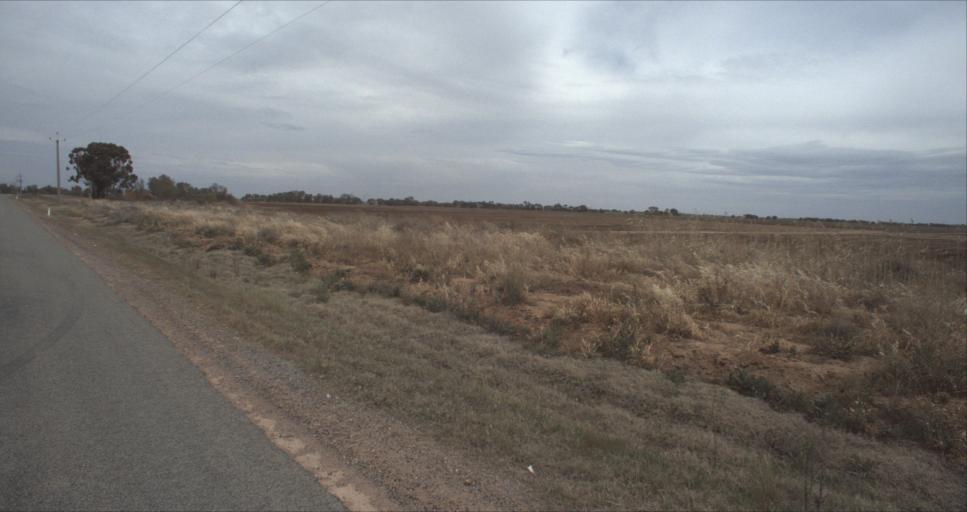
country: AU
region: New South Wales
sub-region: Leeton
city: Leeton
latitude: -34.4353
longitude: 146.3763
